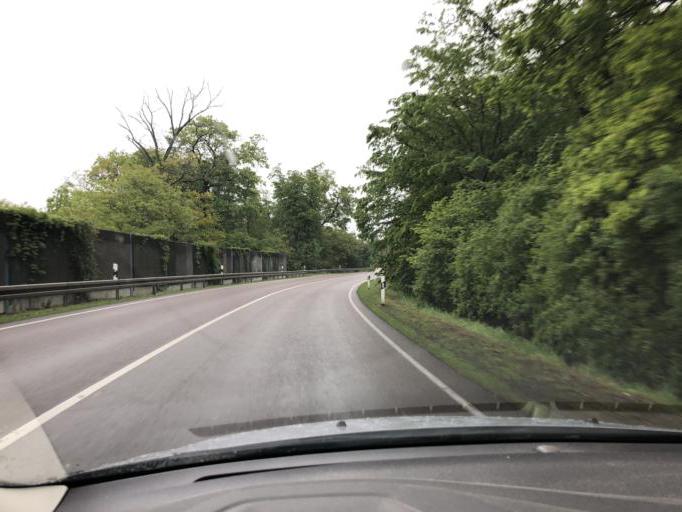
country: DE
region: Saxony-Anhalt
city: Dessau
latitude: 51.8035
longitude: 12.2289
